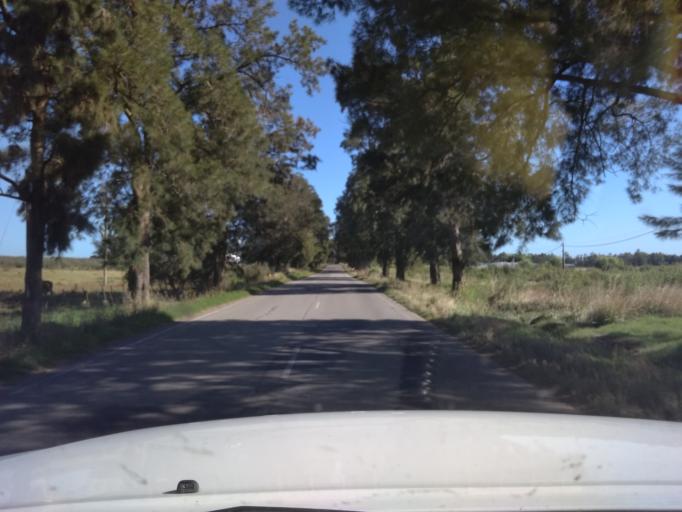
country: UY
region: Canelones
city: San Bautista
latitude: -34.3883
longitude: -55.9595
